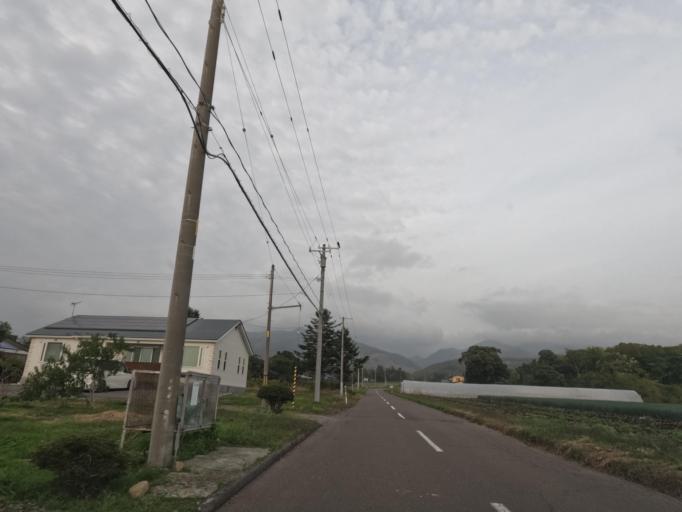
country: JP
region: Hokkaido
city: Date
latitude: 42.4252
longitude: 140.9115
